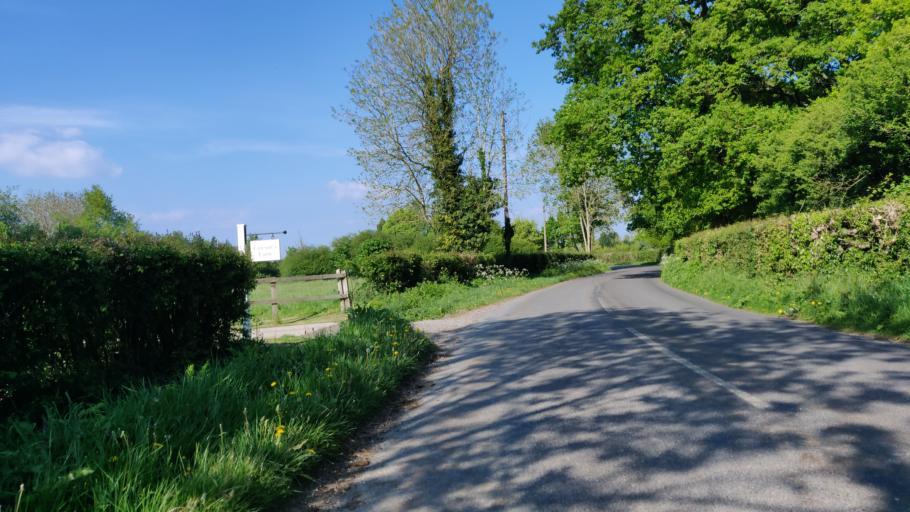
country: GB
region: England
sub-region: West Sussex
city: Southwater
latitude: 51.0306
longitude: -0.3709
